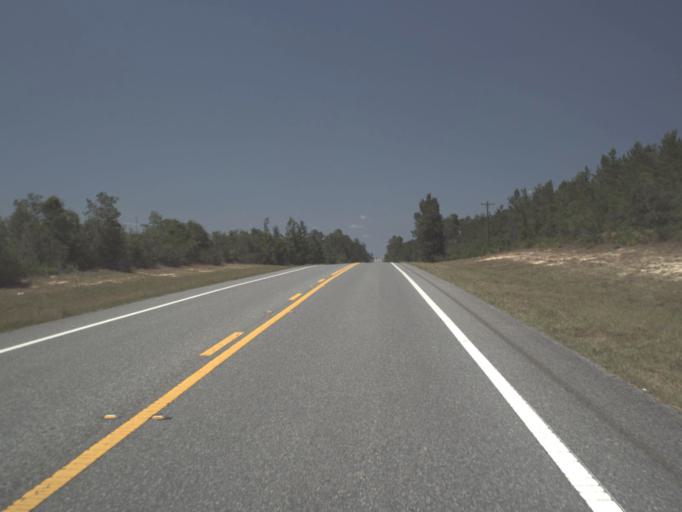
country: US
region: Florida
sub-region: Lake County
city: Astor
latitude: 29.1358
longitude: -81.6258
